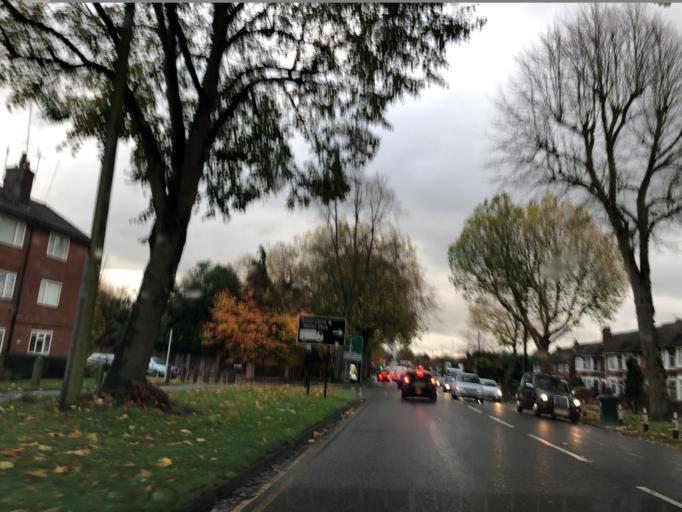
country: GB
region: England
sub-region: Coventry
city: Coventry
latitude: 52.4148
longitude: -1.5339
